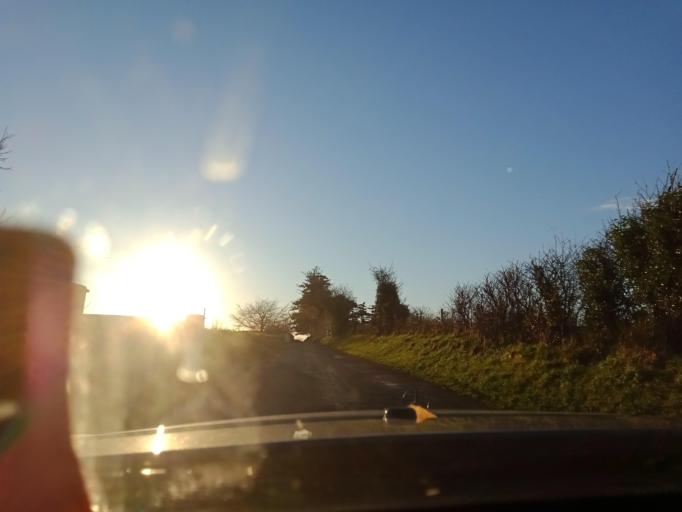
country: IE
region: Leinster
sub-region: Loch Garman
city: New Ross
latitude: 52.3846
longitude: -6.9982
